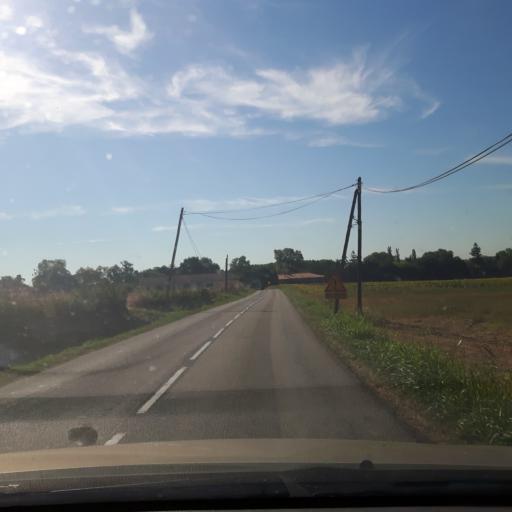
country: FR
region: Midi-Pyrenees
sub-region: Departement de la Haute-Garonne
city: Bouloc
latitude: 43.7653
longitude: 1.4038
